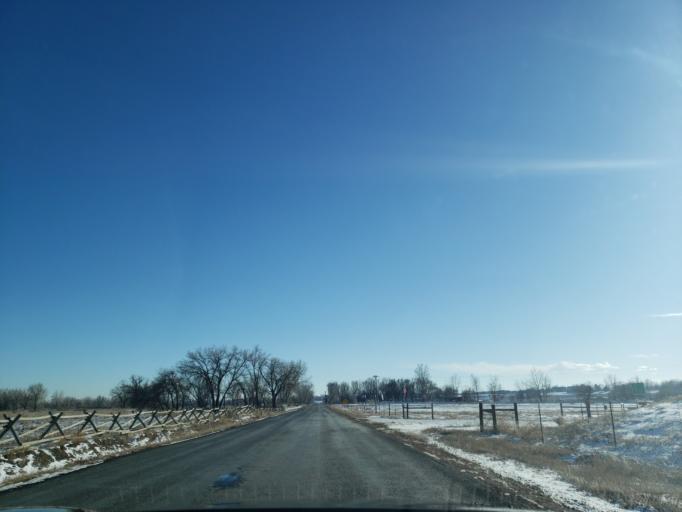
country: US
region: Colorado
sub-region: Larimer County
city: Fort Collins
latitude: 40.5333
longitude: -105.0013
